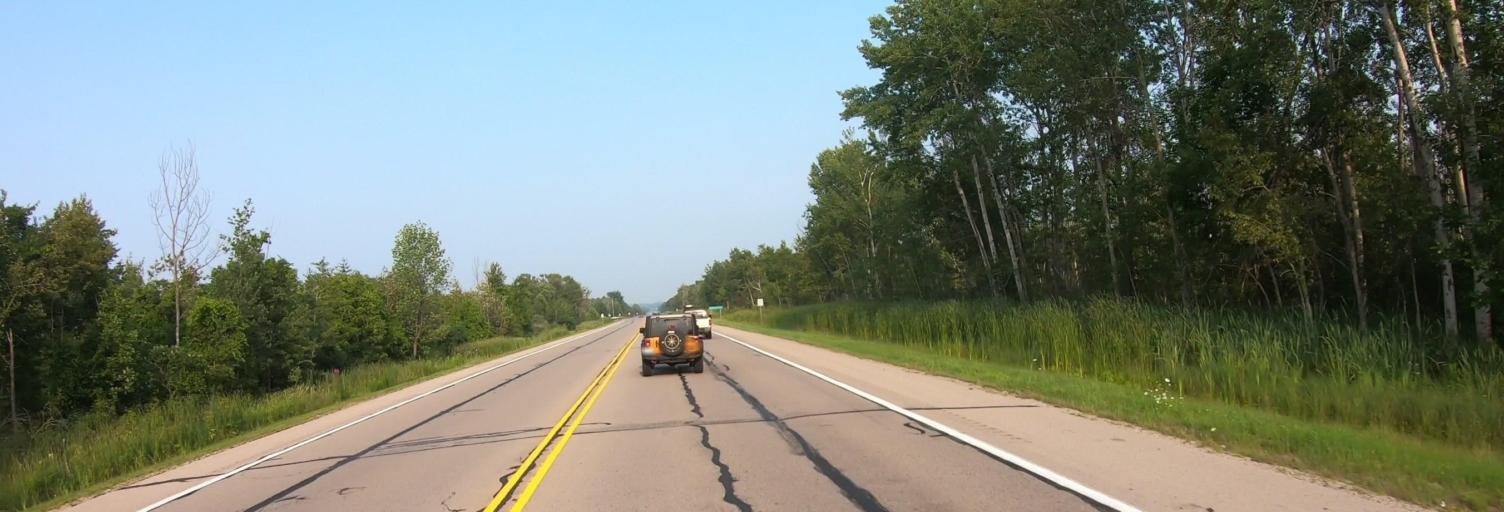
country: US
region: Michigan
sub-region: Emmet County
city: Harbor Springs
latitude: 45.3589
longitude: -85.0808
